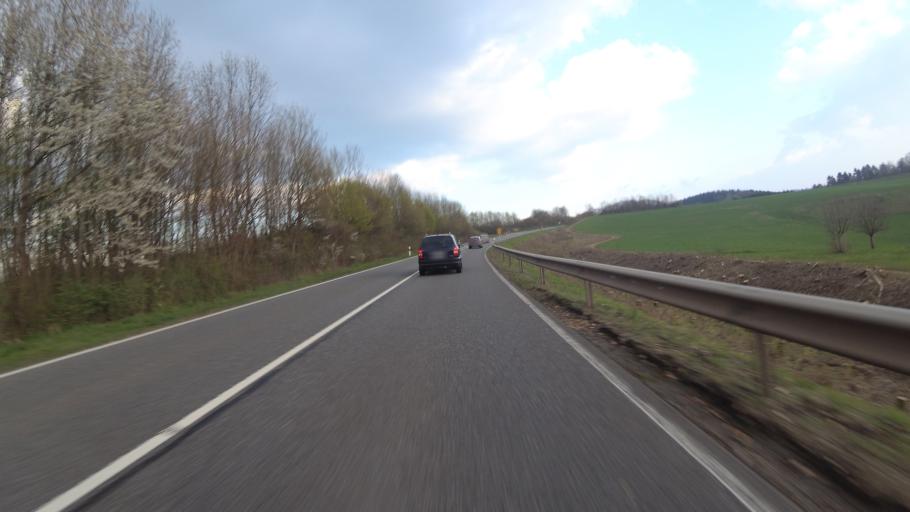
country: DE
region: Rheinland-Pfalz
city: Monzelfeld
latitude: 49.8905
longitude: 7.0602
